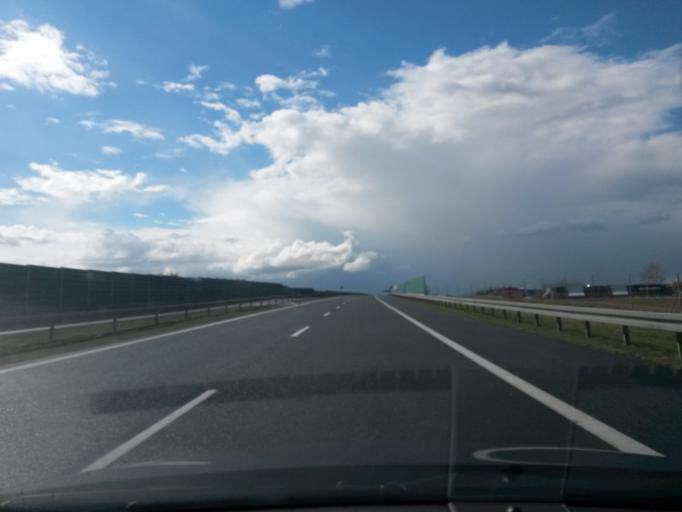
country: PL
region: Greater Poland Voivodeship
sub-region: Powiat wrzesinski
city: Wrzesnia
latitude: 52.3112
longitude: 17.5564
